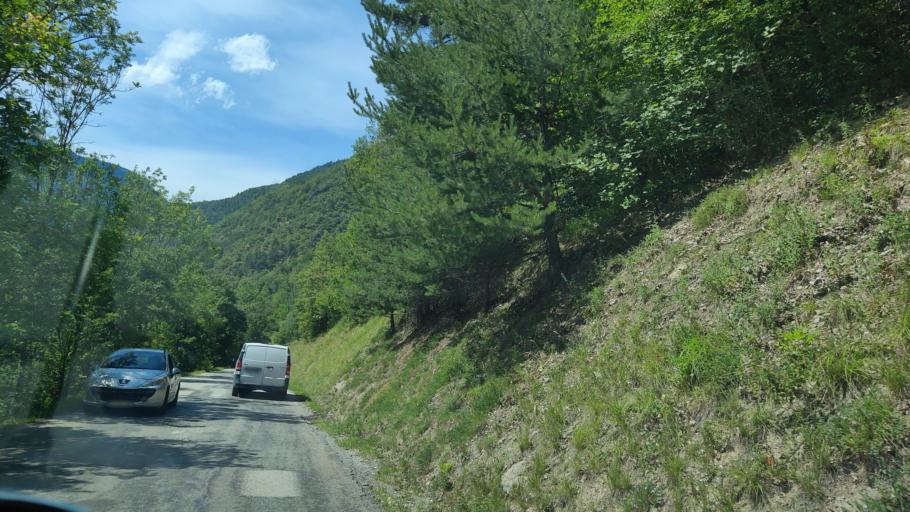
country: FR
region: Rhone-Alpes
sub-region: Departement de la Savoie
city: Salins-les-Thermes
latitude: 45.4615
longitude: 6.5528
